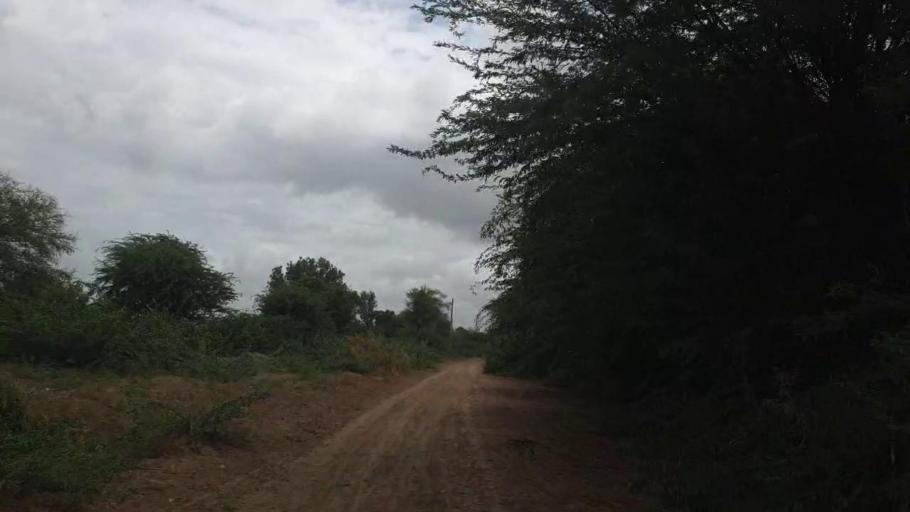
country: PK
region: Sindh
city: Badin
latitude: 24.6347
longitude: 68.9485
